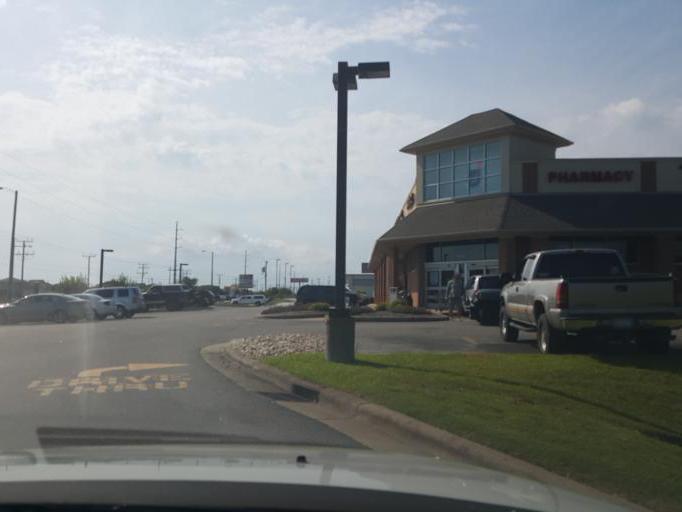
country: US
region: North Carolina
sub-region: Dare County
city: Kill Devil Hills
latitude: 36.0040
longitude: -75.6555
